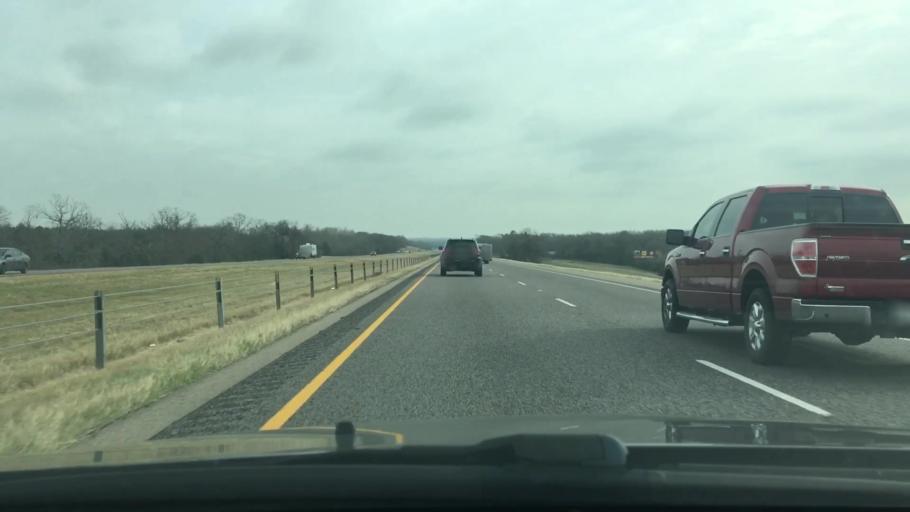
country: US
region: Texas
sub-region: Leon County
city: Buffalo
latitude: 31.5257
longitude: -96.1134
